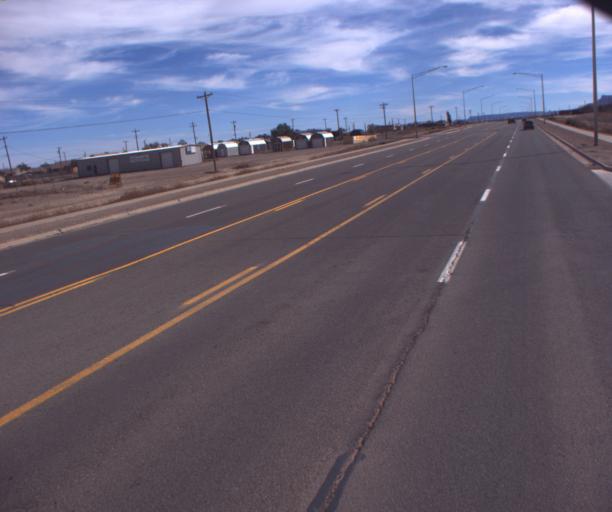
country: US
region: Arizona
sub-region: Navajo County
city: Kayenta
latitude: 36.7163
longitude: -110.2528
